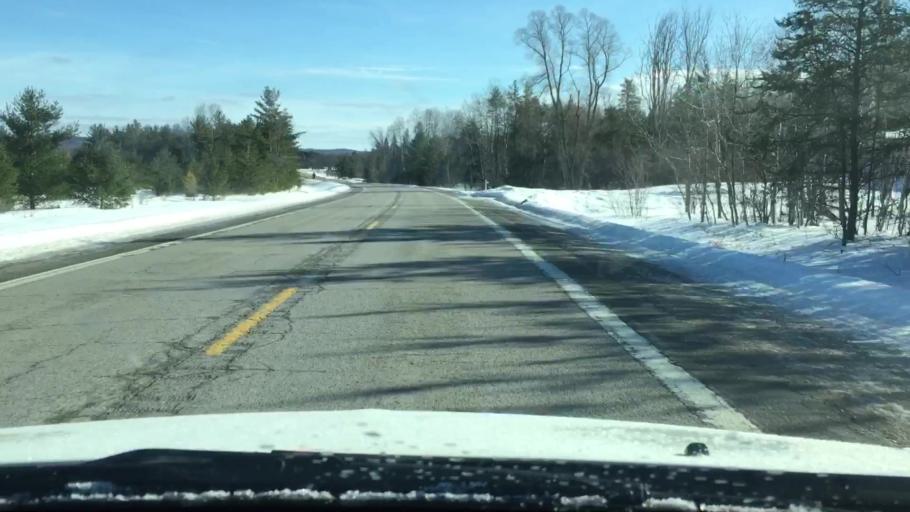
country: US
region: Michigan
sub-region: Charlevoix County
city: East Jordan
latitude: 45.1057
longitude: -85.1240
